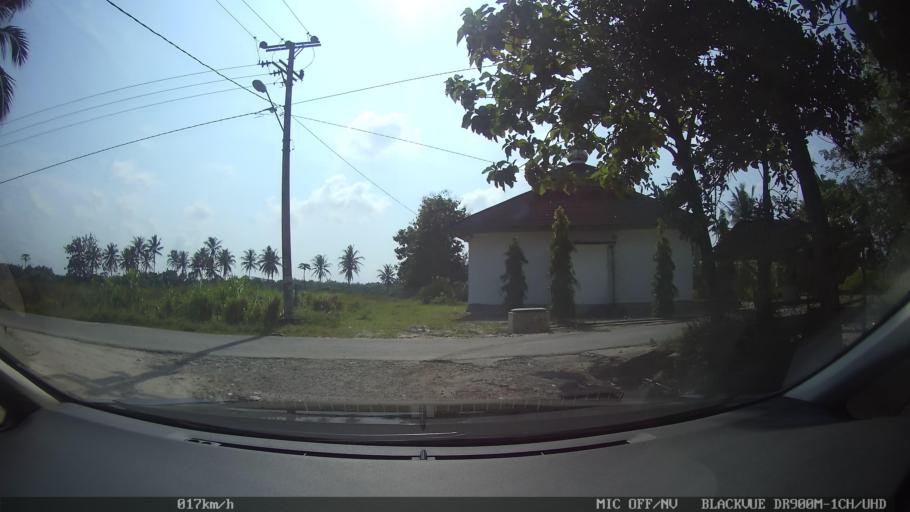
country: ID
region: Lampung
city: Natar
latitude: -5.2645
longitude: 105.2134
